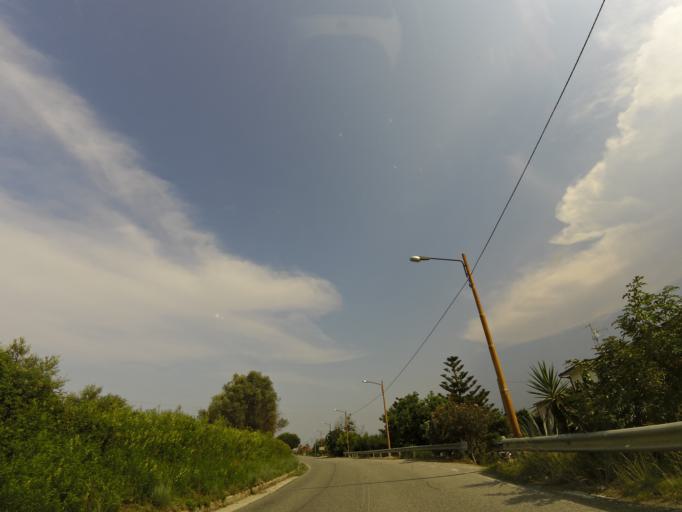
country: IT
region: Calabria
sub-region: Provincia di Reggio Calabria
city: Monasterace
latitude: 38.4461
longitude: 16.5350
